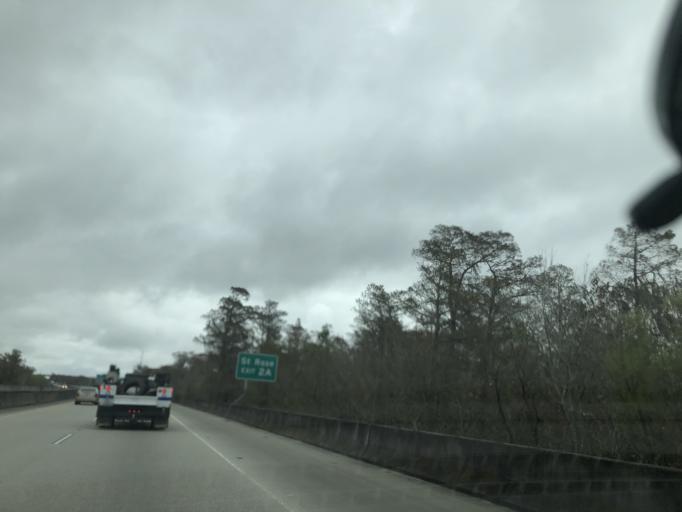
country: US
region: Louisiana
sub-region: Saint Charles Parish
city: Saint Rose
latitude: 29.9688
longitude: -90.3287
